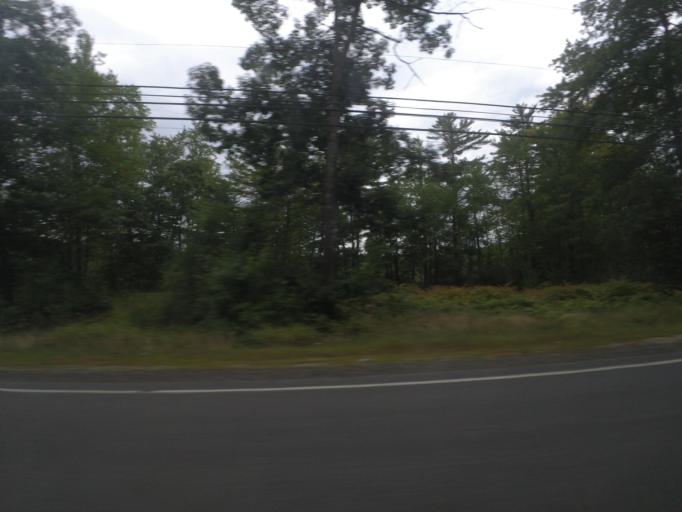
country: US
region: New Hampshire
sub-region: Strafford County
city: Rochester
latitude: 43.2841
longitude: -71.0070
